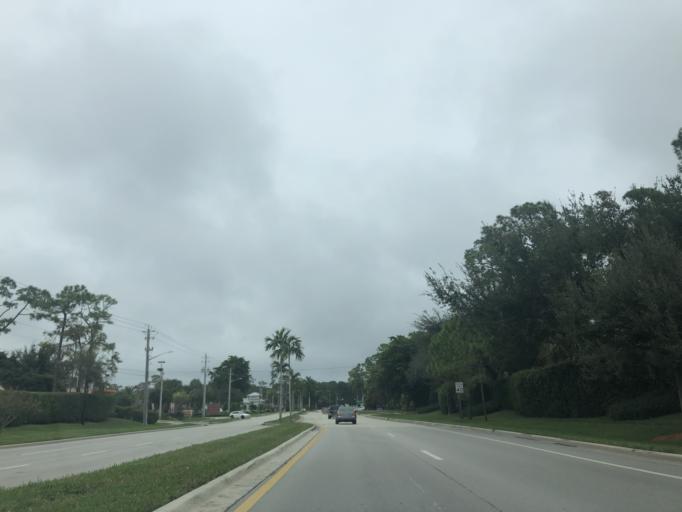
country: US
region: Florida
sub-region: Palm Beach County
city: Wellington
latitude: 26.6702
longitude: -80.2465
